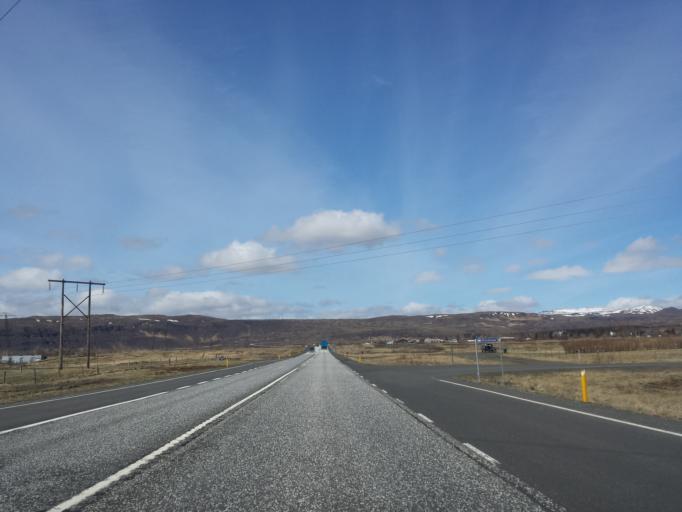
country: IS
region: South
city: Hveragerdi
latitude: 63.9879
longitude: -21.1672
